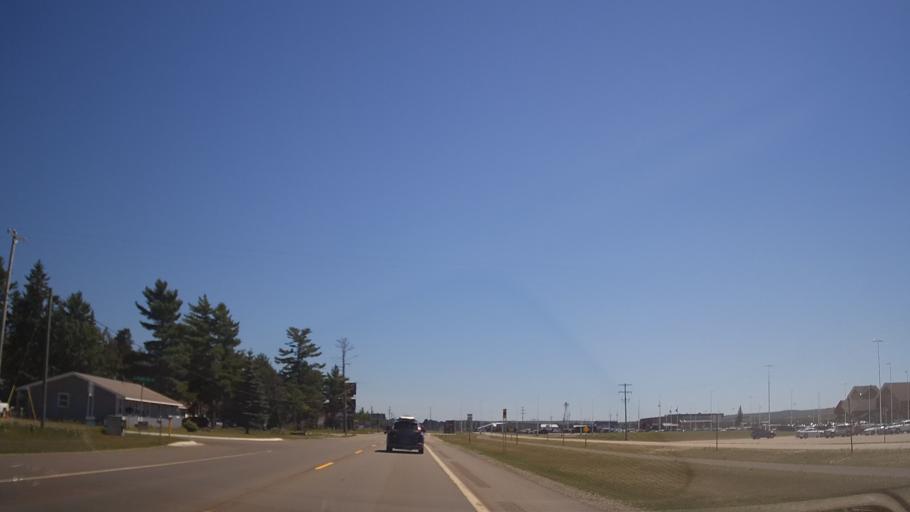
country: US
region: Michigan
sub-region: Cheboygan County
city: Indian River
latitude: 45.5736
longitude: -84.7837
